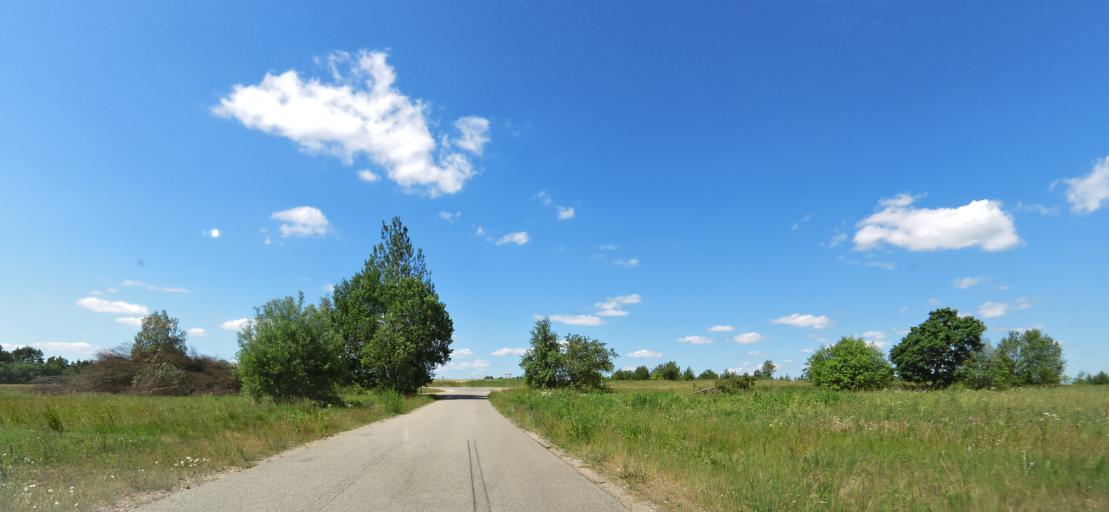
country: LT
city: Nemencine
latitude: 54.8787
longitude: 25.5304
